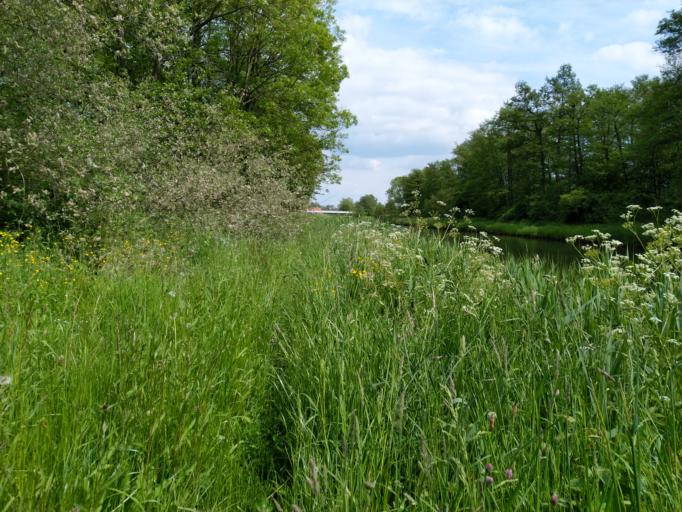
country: FR
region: Picardie
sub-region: Departement de l'Aisne
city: Boue
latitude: 50.0403
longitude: 3.6570
